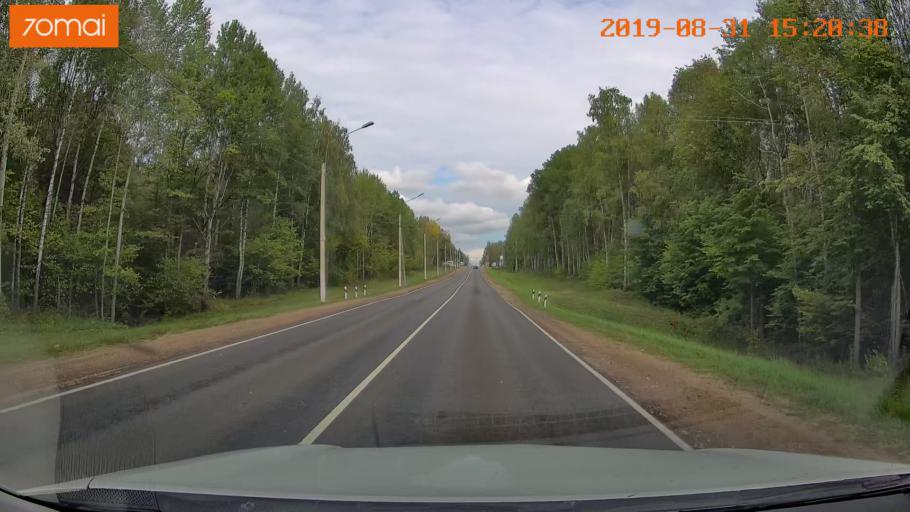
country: RU
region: Kaluga
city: Baryatino
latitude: 54.4913
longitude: 34.4398
